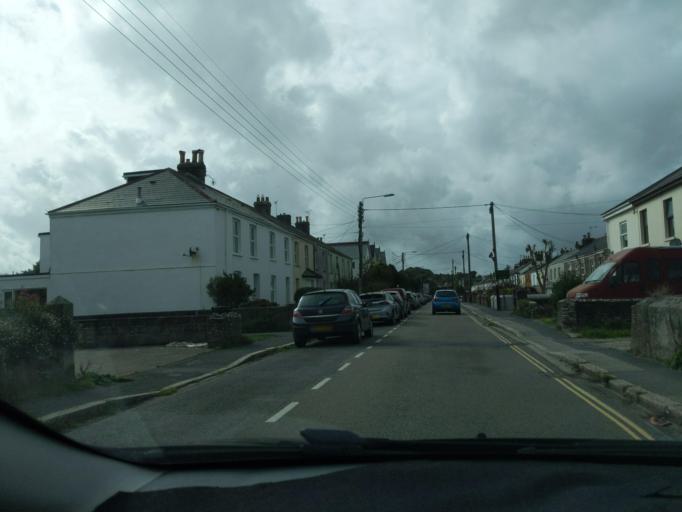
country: GB
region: England
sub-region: Cornwall
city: Par
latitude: 50.3512
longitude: -4.7020
